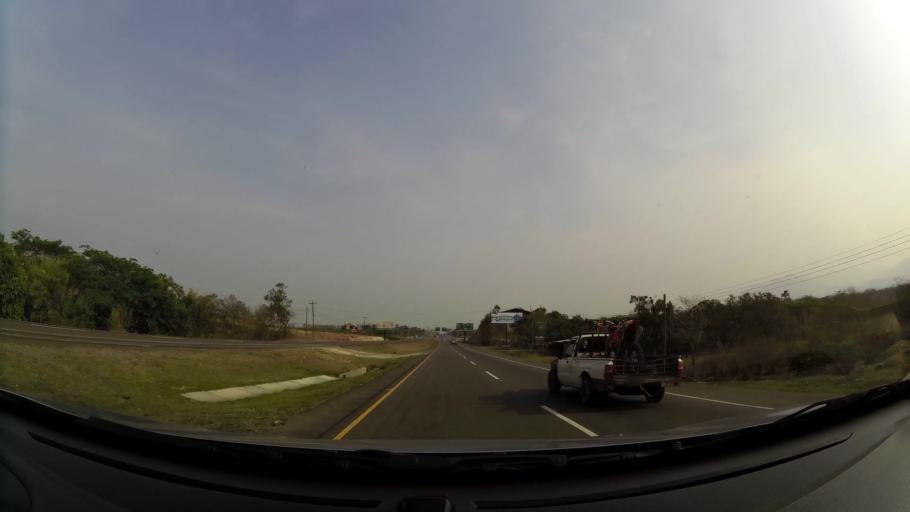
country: HN
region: Comayagua
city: Villa de San Antonio
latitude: 14.3447
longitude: -87.5941
